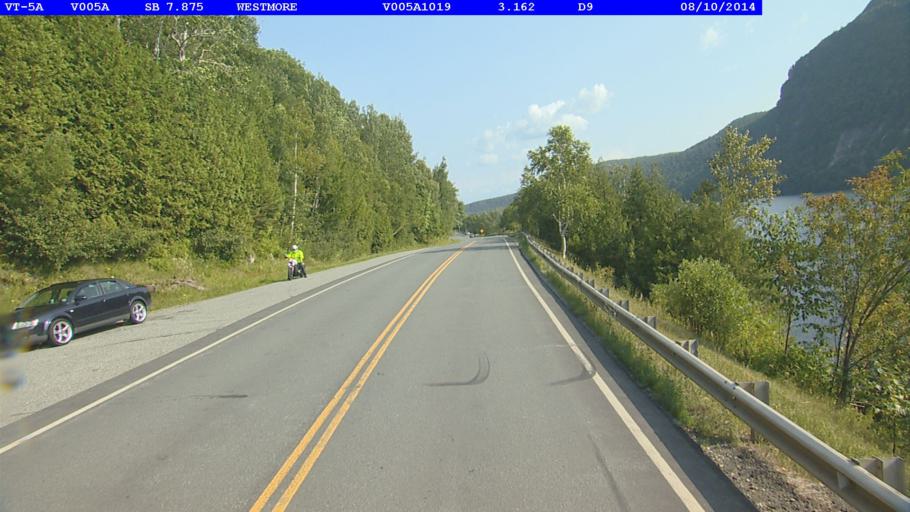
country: US
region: Vermont
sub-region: Caledonia County
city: Lyndonville
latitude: 44.7369
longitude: -72.0451
